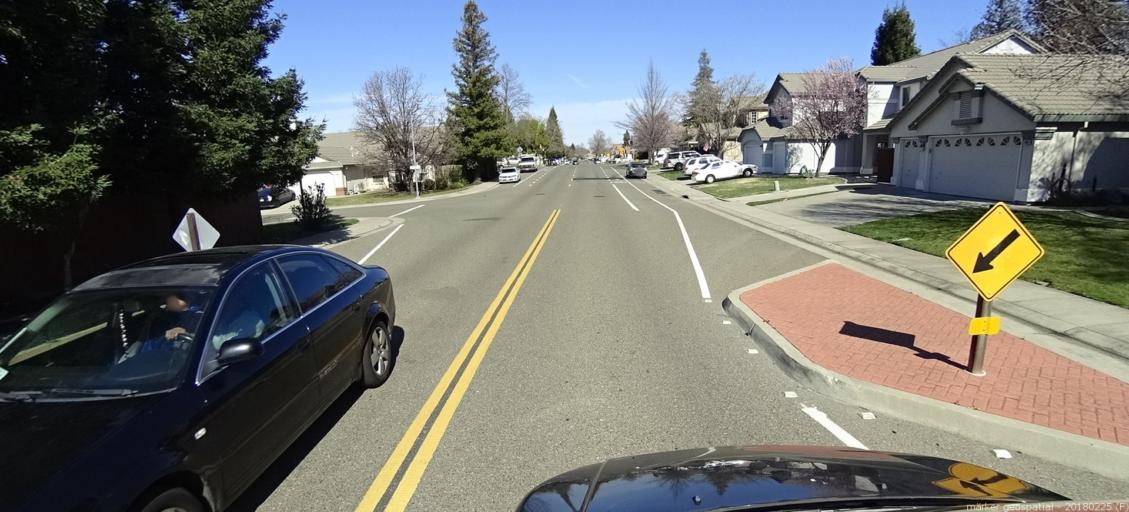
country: US
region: California
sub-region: Sacramento County
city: Antelope
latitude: 38.7144
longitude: -121.3396
